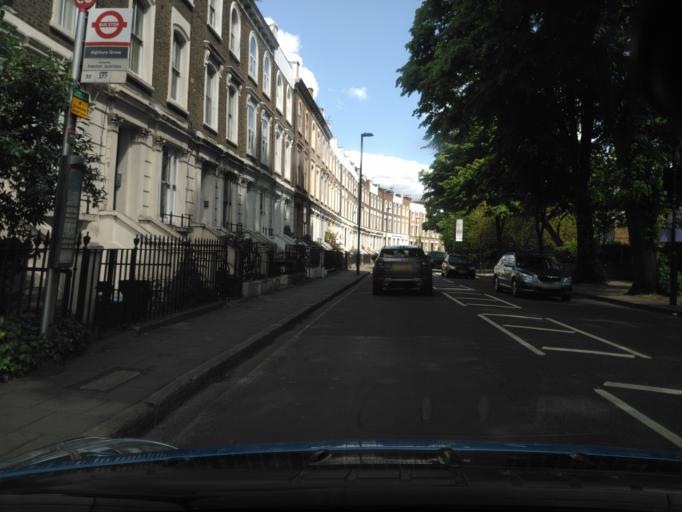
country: GB
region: England
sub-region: Greater London
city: Islington
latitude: 51.5469
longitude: -0.0979
